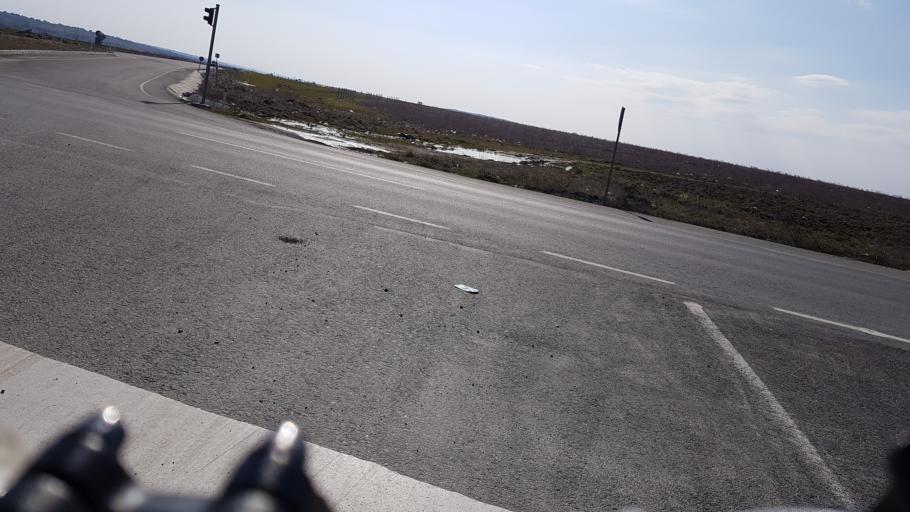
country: TR
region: Tekirdag
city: Saray
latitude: 41.4315
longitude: 27.9094
